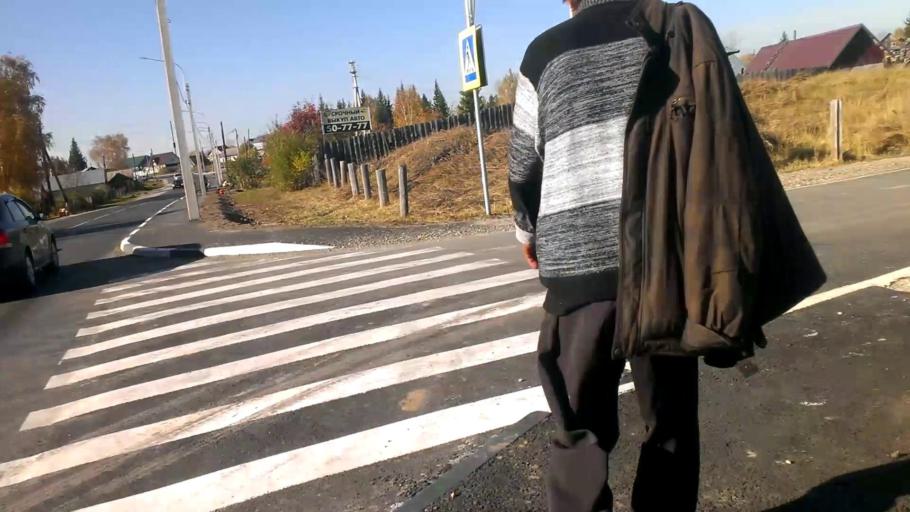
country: RU
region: Altai Krai
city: Sannikovo
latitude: 53.3146
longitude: 83.9608
